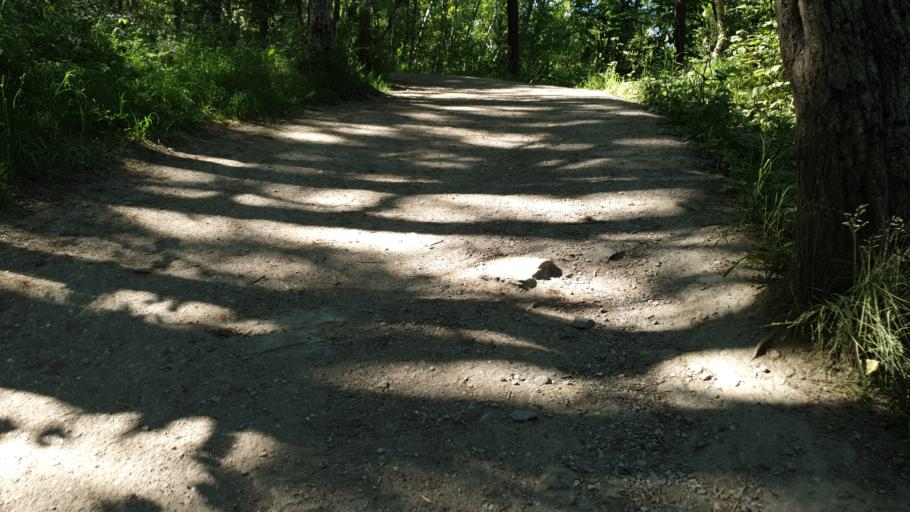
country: NO
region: Sor-Trondelag
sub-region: Trondheim
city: Trondheim
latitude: 63.4540
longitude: 10.4593
